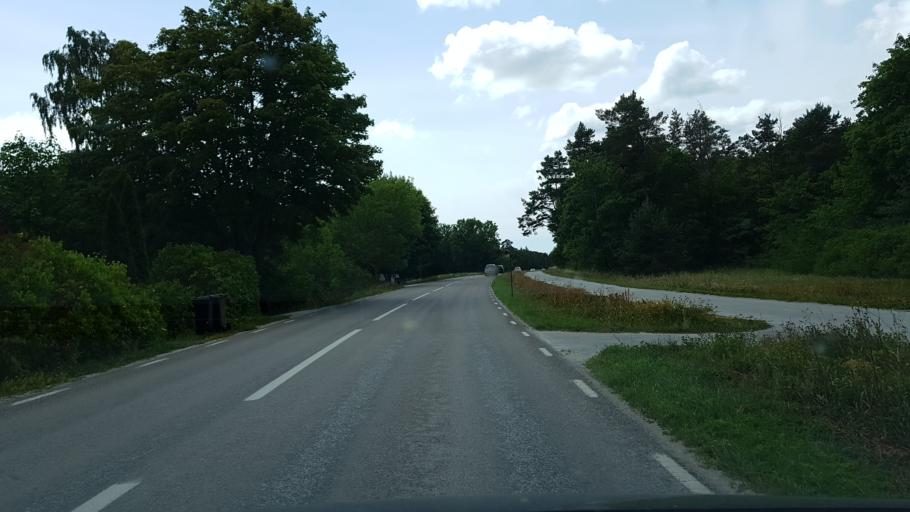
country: SE
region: Gotland
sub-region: Gotland
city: Visby
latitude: 57.7483
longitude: 18.4203
